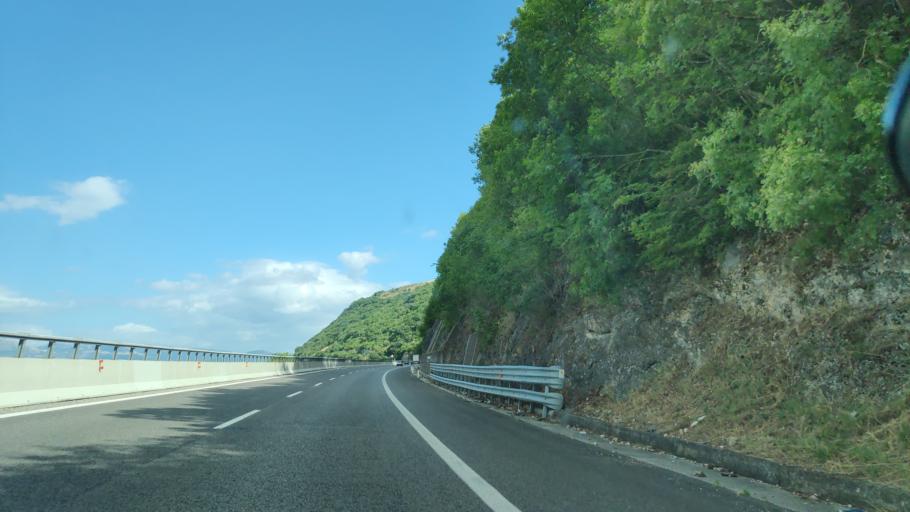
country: IT
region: Campania
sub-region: Provincia di Salerno
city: Sicignano degli Alburni
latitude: 40.5959
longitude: 15.3210
